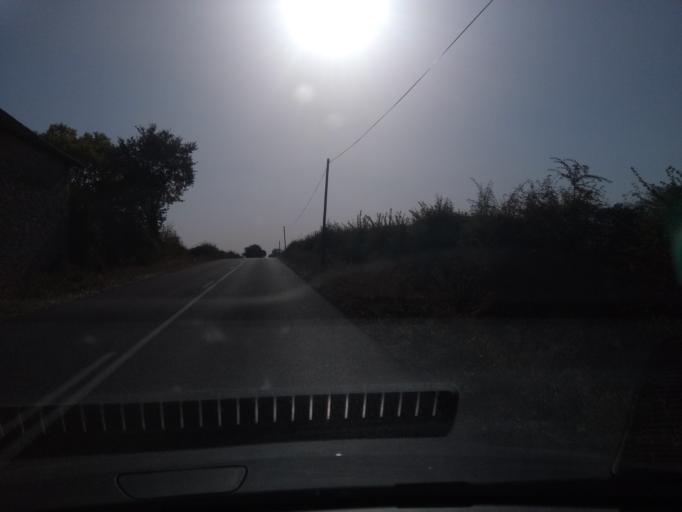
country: FR
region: Poitou-Charentes
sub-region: Departement de la Vienne
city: Lathus-Saint-Remy
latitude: 46.4597
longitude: 1.0291
